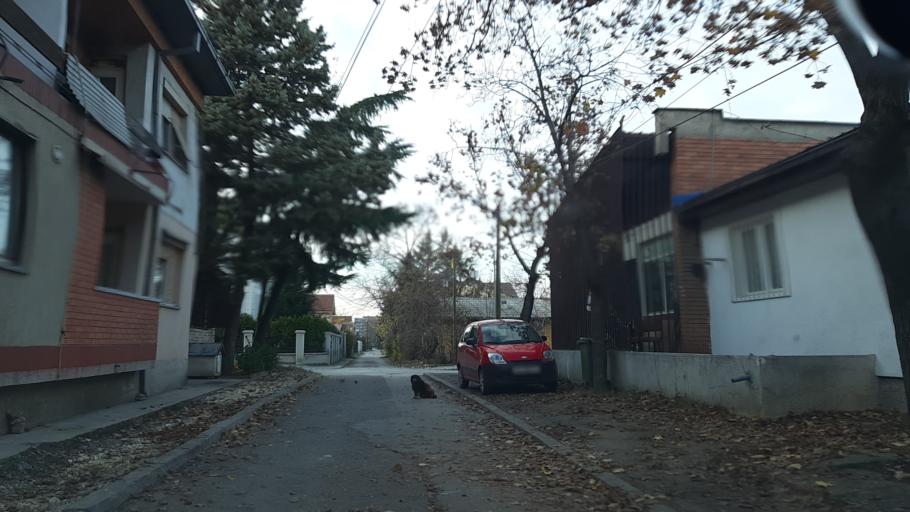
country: MK
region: Kisela Voda
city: Usje
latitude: 41.9757
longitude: 21.4538
